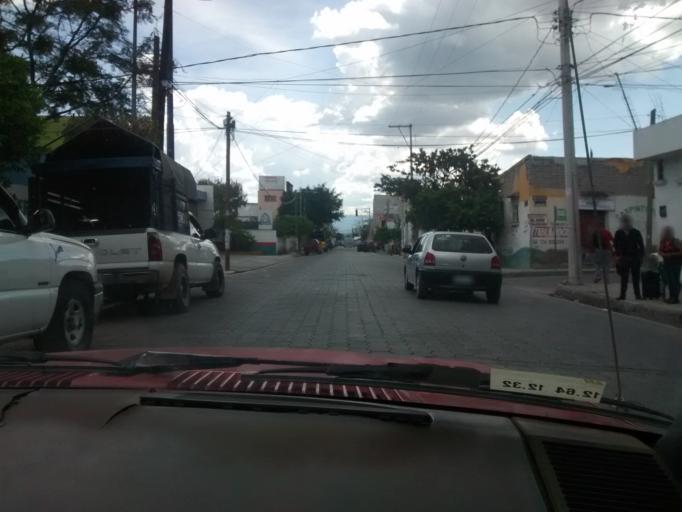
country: MX
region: Puebla
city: Tehuacan
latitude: 18.4616
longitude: -97.3850
